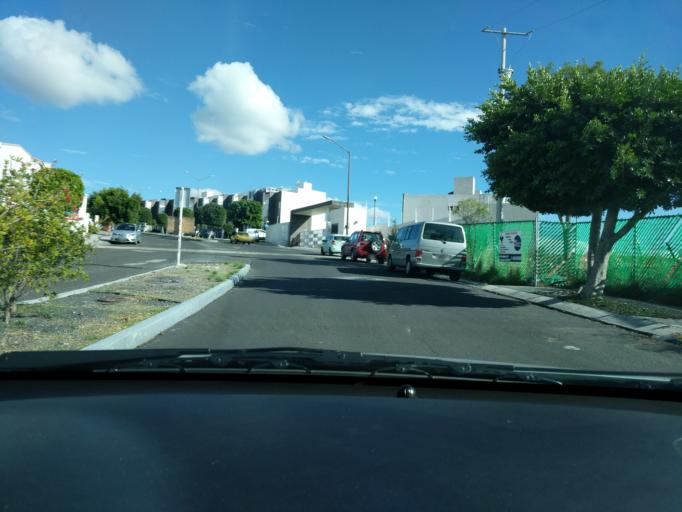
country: MX
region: Queretaro
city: La Canada
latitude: 20.5863
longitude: -100.3384
